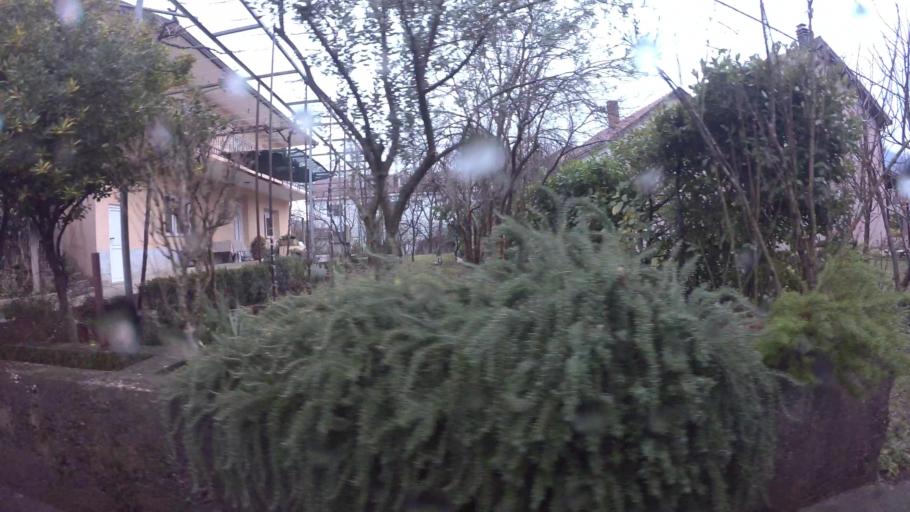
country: BA
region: Federation of Bosnia and Herzegovina
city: Cim
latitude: 43.3521
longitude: 17.7806
